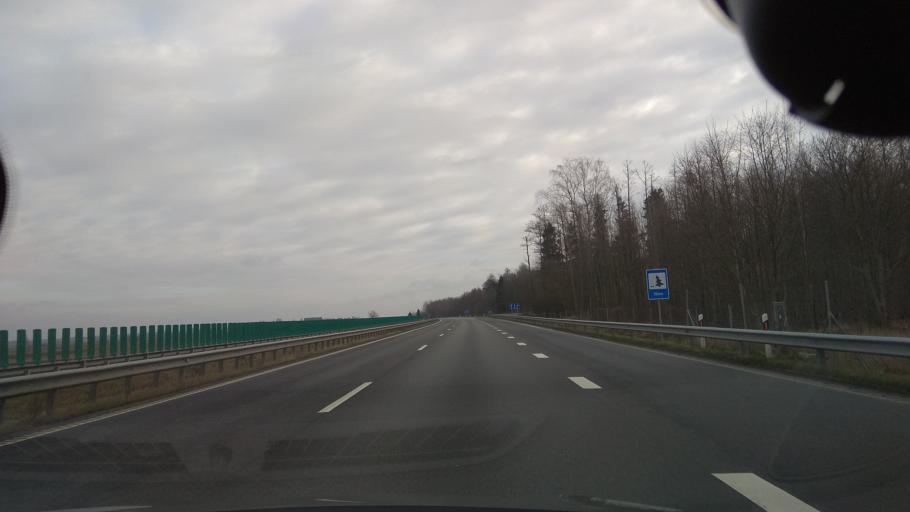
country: LT
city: Kazlu Ruda
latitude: 54.6759
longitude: 23.5610
